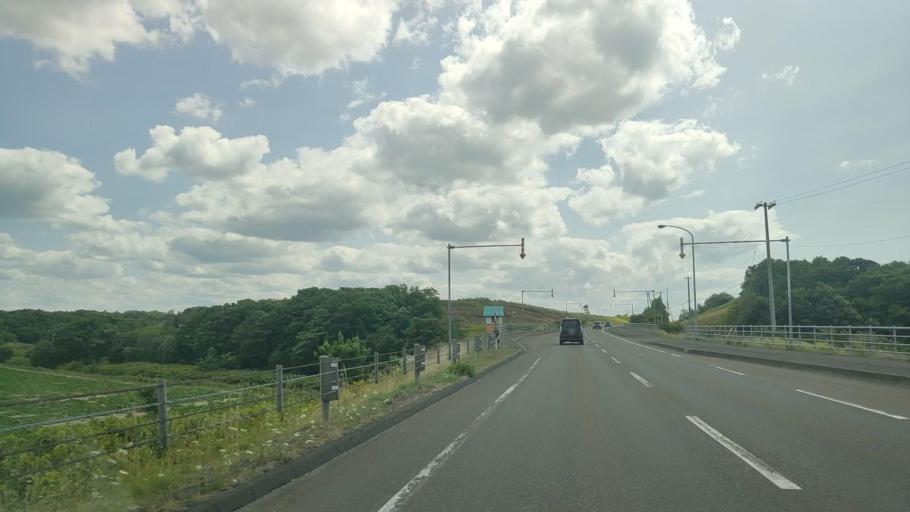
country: JP
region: Hokkaido
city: Makubetsu
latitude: 44.7931
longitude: 141.7899
